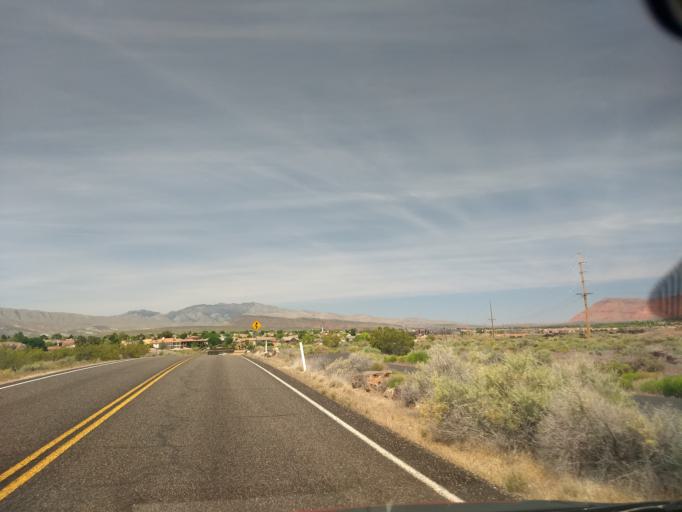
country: US
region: Utah
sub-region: Washington County
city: Santa Clara
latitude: 37.1440
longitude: -113.6488
